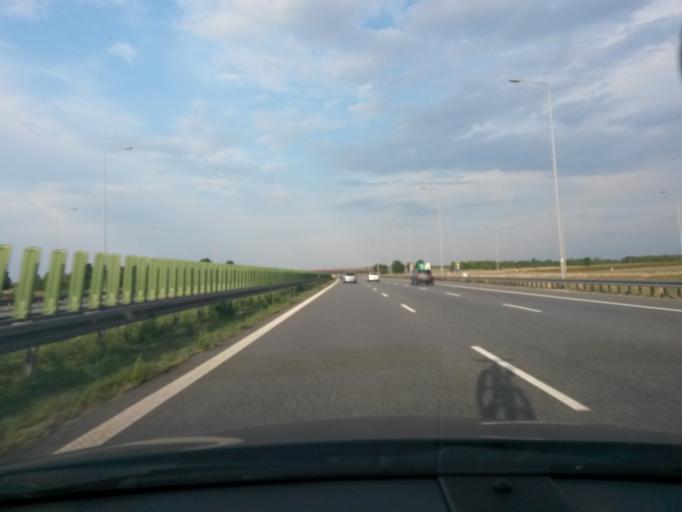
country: PL
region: Lodz Voivodeship
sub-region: Powiat zgierski
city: Strykow
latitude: 51.8921
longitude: 19.6428
